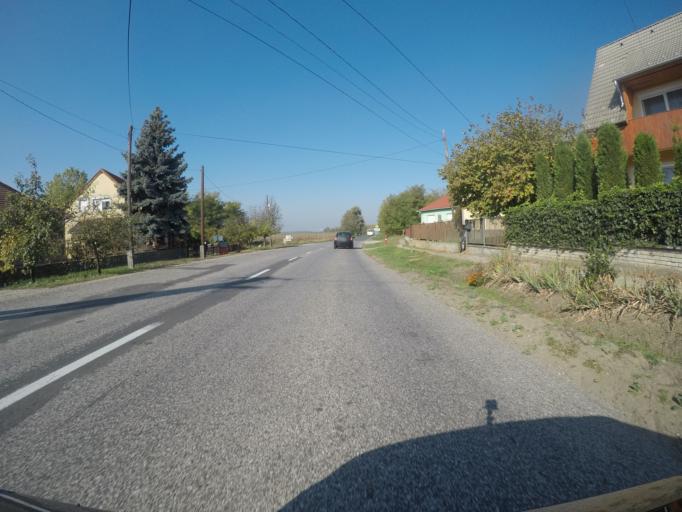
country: HU
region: Tolna
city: Szedres
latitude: 46.4876
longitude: 18.6797
